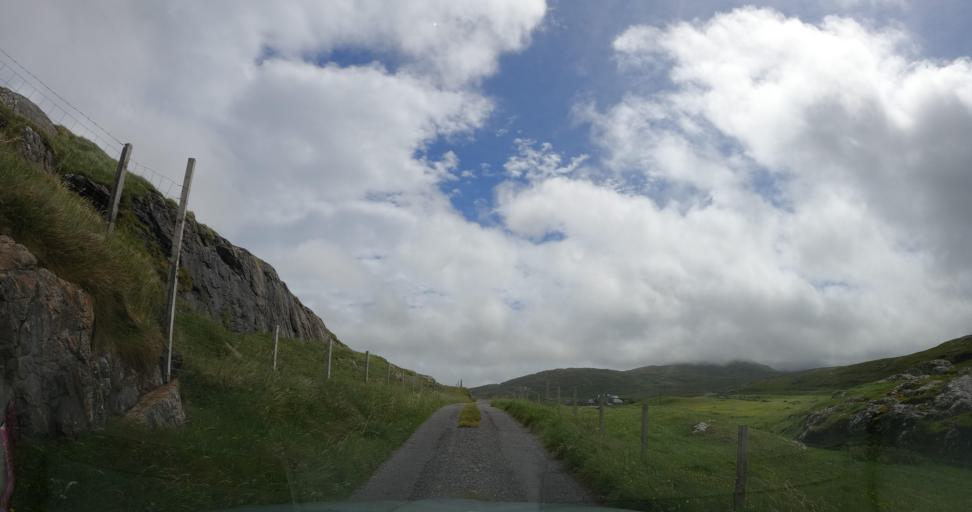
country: GB
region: Scotland
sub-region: Eilean Siar
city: Barra
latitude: 57.0048
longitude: -7.4949
